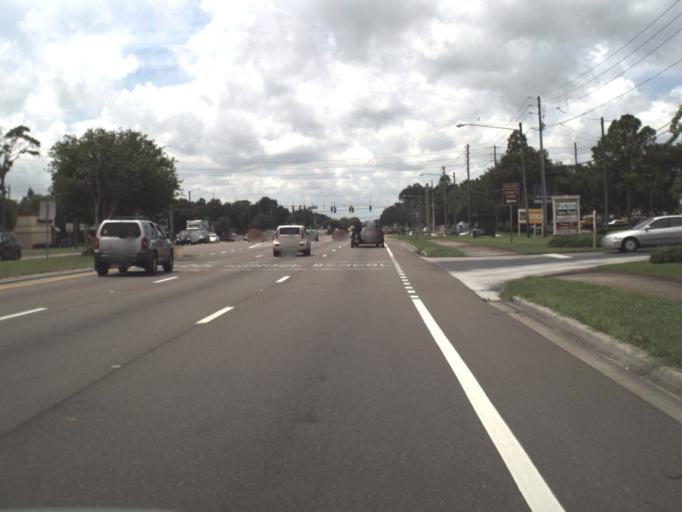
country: US
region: Florida
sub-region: Pinellas County
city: Safety Harbor
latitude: 28.0138
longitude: -82.7091
